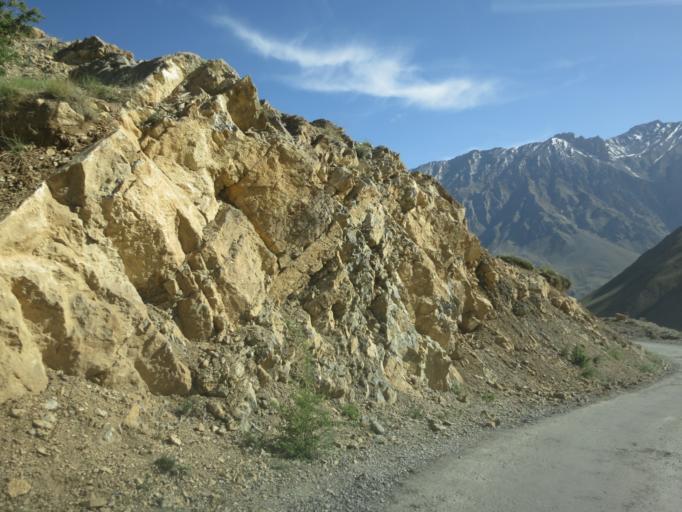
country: IN
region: Himachal Pradesh
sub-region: Kulu
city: Manali
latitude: 32.3229
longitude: 78.0031
